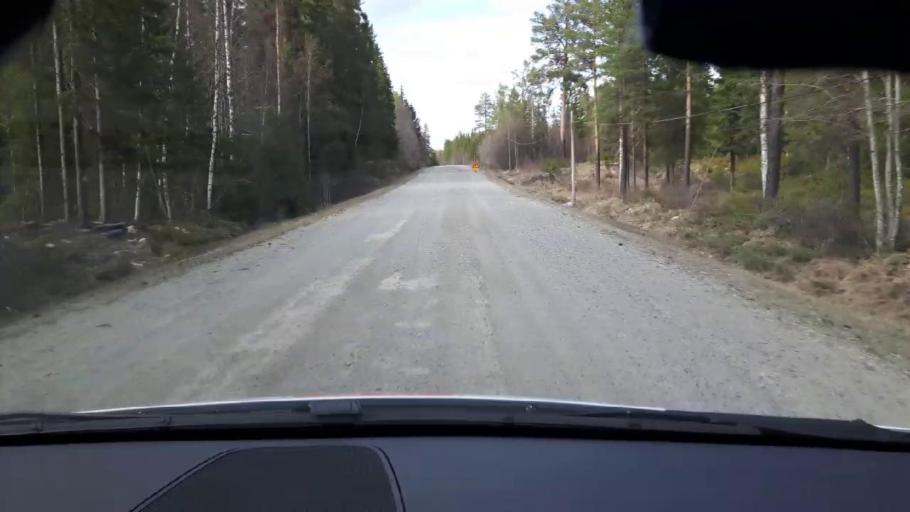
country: SE
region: Jaemtland
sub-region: Bergs Kommun
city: Hoverberg
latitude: 62.6708
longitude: 14.7462
